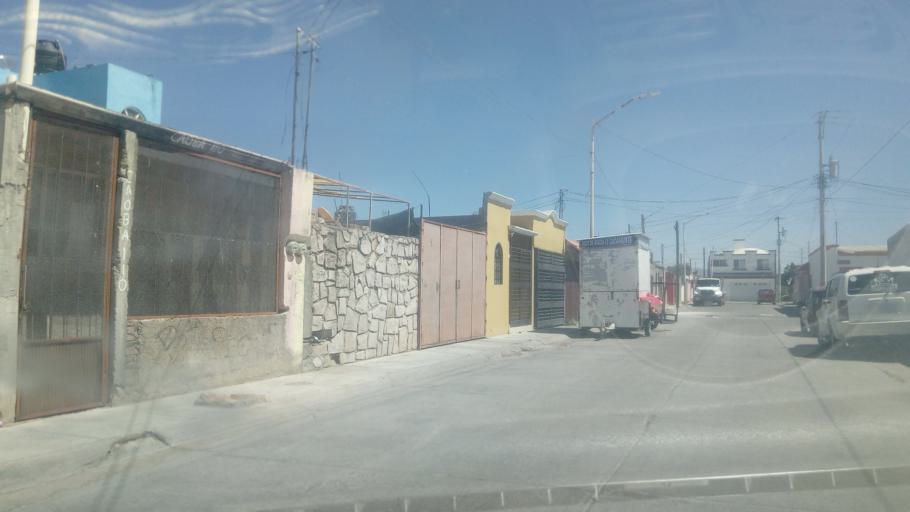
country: MX
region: Durango
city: Victoria de Durango
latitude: 24.0046
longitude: -104.6246
